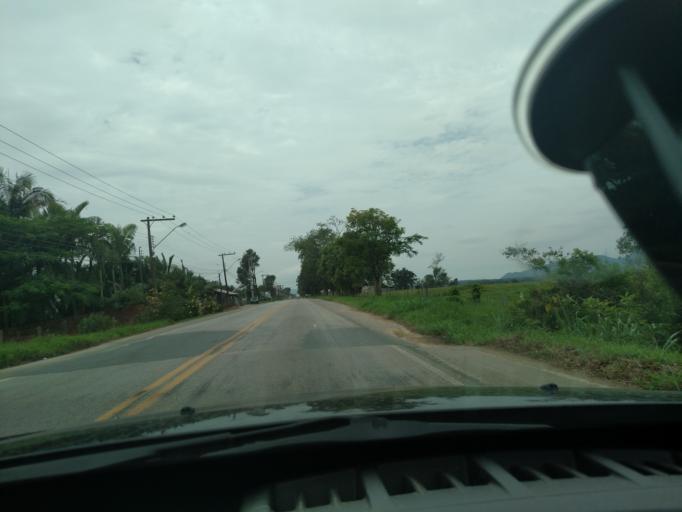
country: BR
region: Santa Catarina
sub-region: Gaspar
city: Gaspar
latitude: -26.8883
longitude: -48.8147
